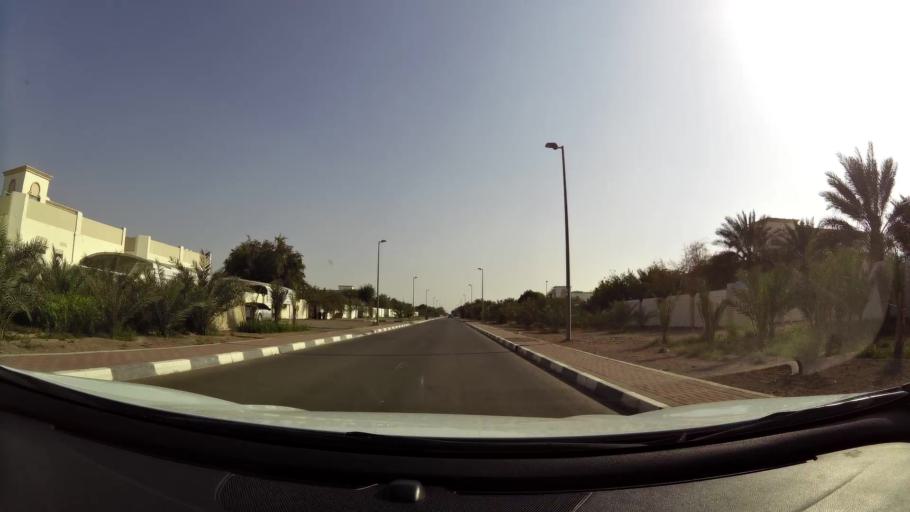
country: AE
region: Abu Dhabi
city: Al Ain
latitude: 24.0808
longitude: 55.8630
